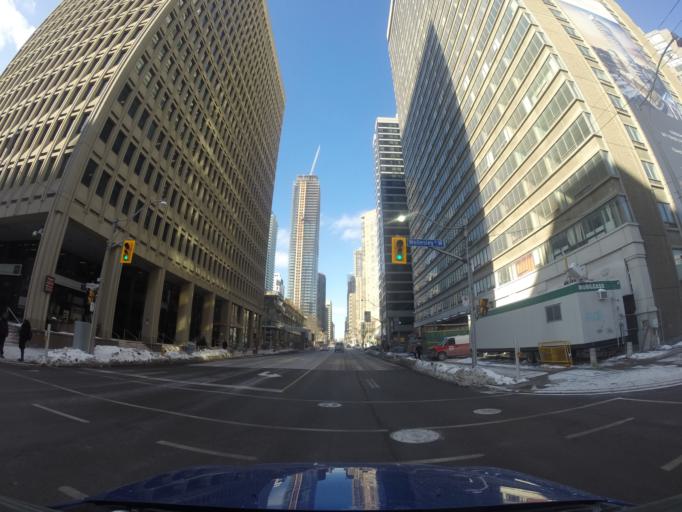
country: CA
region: Ontario
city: Toronto
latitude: 43.6643
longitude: -79.3870
